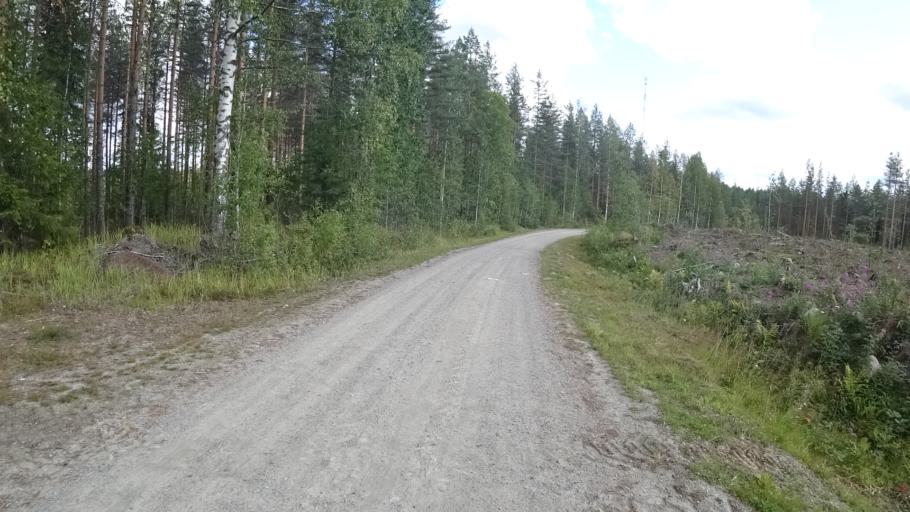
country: FI
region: North Karelia
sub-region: Joensuu
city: Ilomantsi
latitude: 62.6191
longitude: 31.2282
